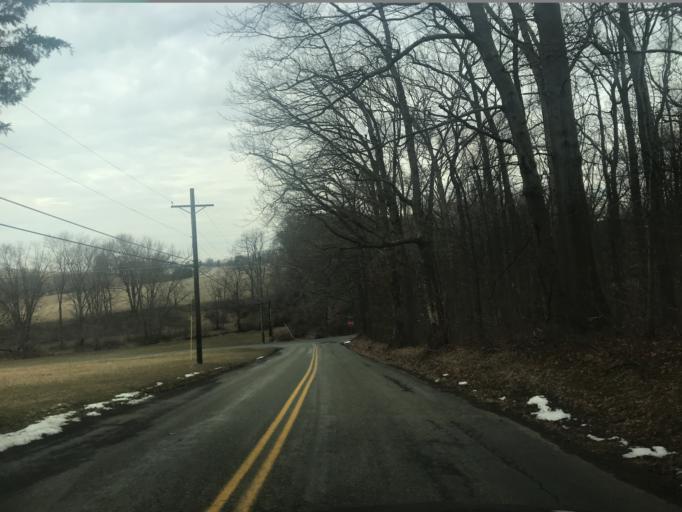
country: US
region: Maryland
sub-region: Harford County
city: Jarrettsville
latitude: 39.6570
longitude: -76.4054
